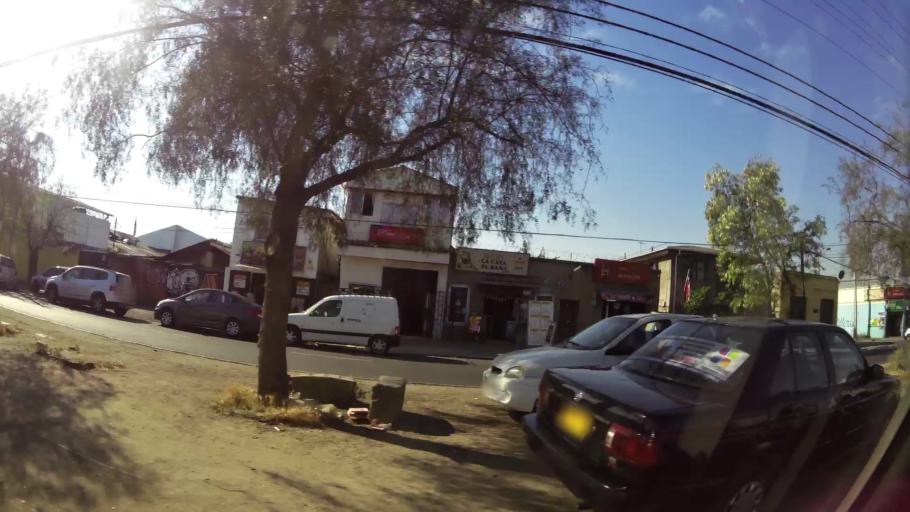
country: CL
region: Santiago Metropolitan
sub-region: Provincia de Santiago
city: Santiago
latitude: -33.4789
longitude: -70.6584
